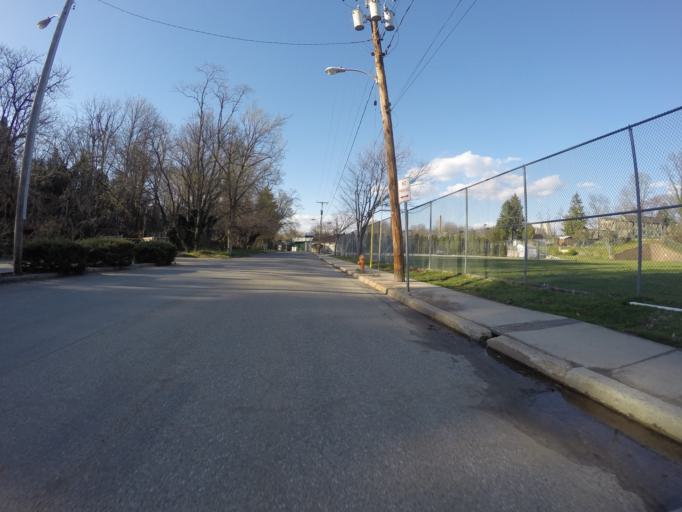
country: US
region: Maryland
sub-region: Baltimore County
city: Towson
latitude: 39.3544
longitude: -76.6294
